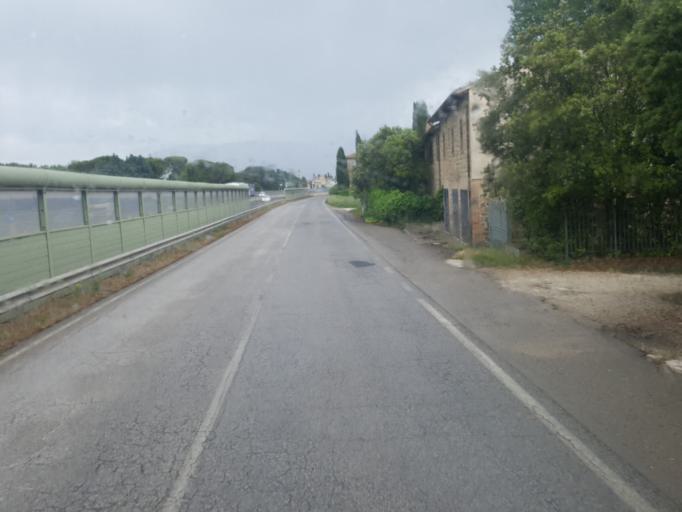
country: IT
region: Umbria
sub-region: Provincia di Perugia
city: Ospedalicchio
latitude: 43.0813
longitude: 12.4935
